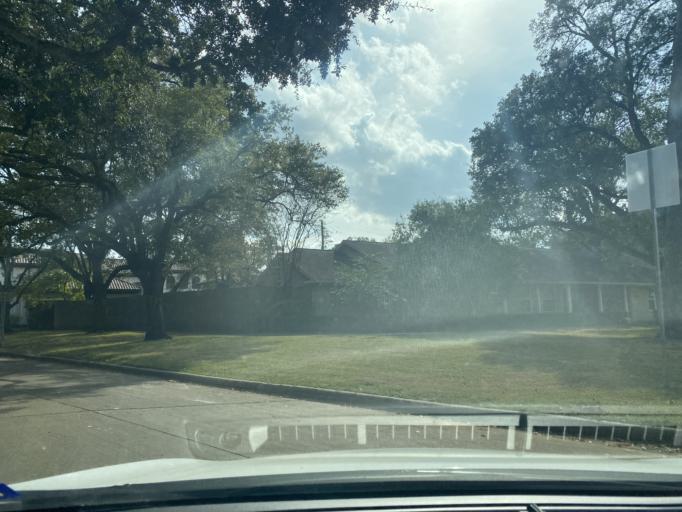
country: US
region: Texas
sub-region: Harris County
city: Hunters Creek Village
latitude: 29.7587
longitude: -95.4744
